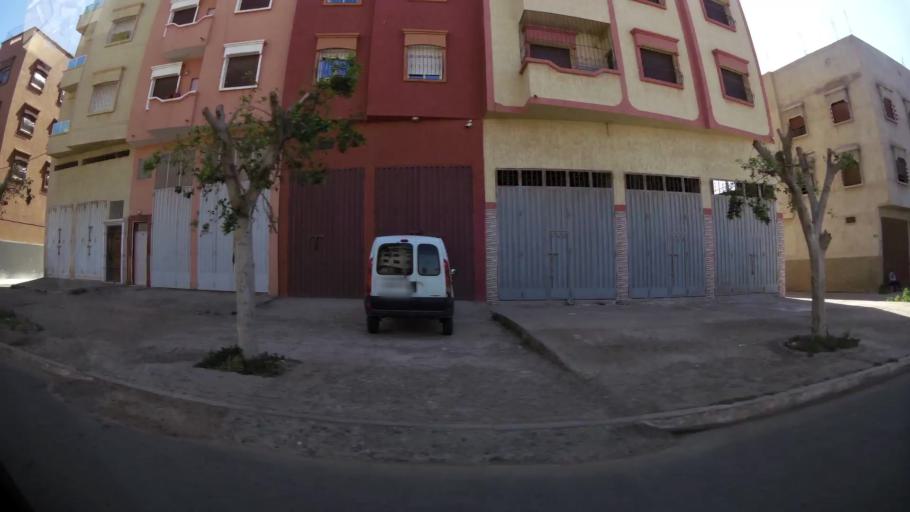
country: MA
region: Souss-Massa-Draa
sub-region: Inezgane-Ait Mellou
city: Inezgane
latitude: 30.3444
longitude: -9.5077
